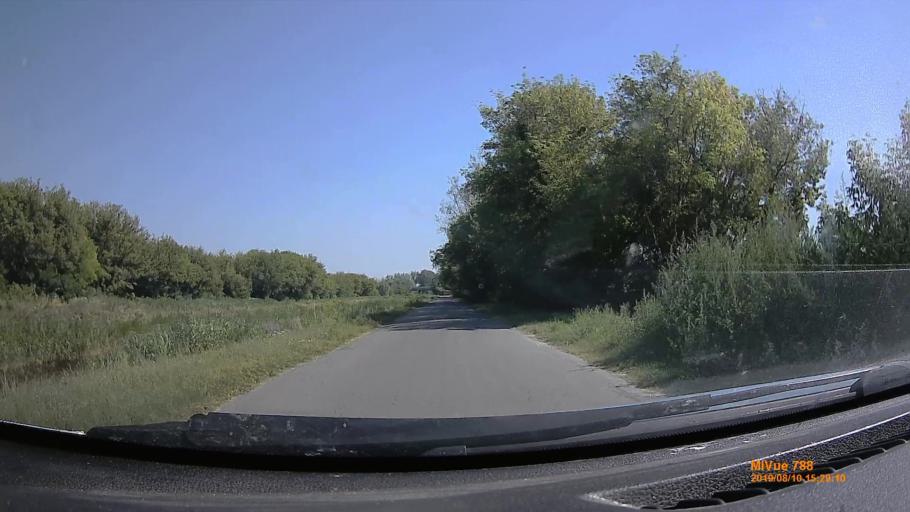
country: HU
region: Somogy
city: Balatonfenyves
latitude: 46.7070
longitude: 17.4808
